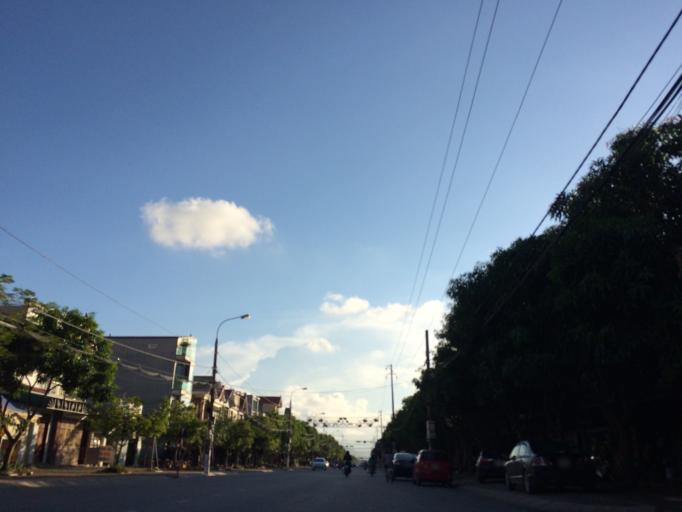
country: VN
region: Ha Tinh
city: Ha Tinh
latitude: 18.3491
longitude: 105.8971
